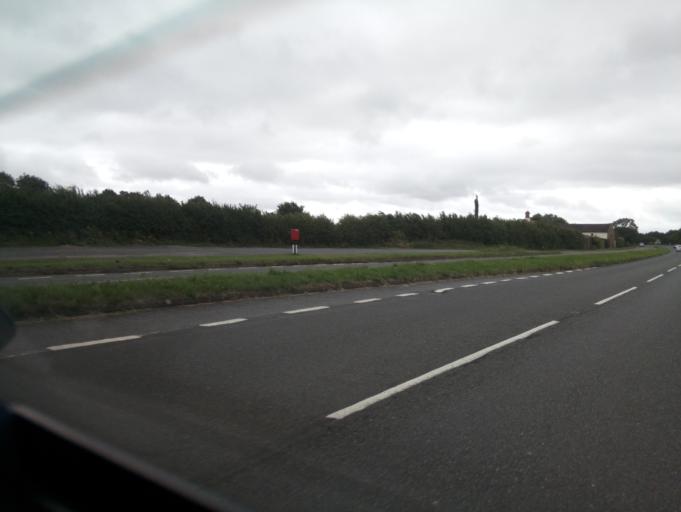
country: GB
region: England
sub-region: Gloucestershire
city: Tewkesbury
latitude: 51.9531
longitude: -2.1587
